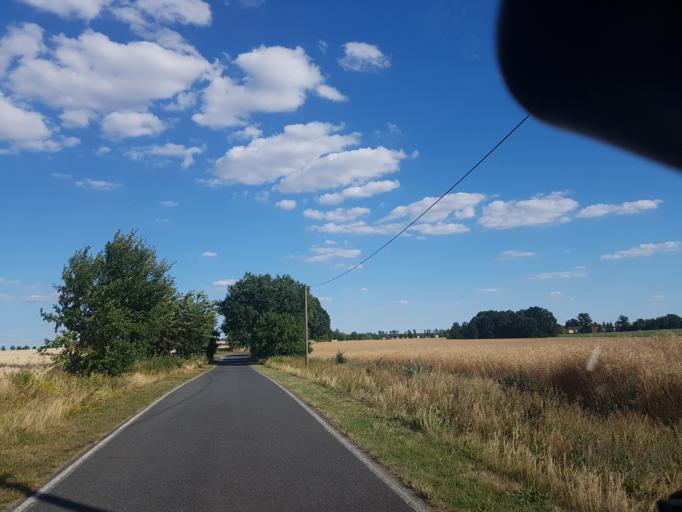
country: DE
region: Brandenburg
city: Juterbog
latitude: 51.9222
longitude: 13.1472
